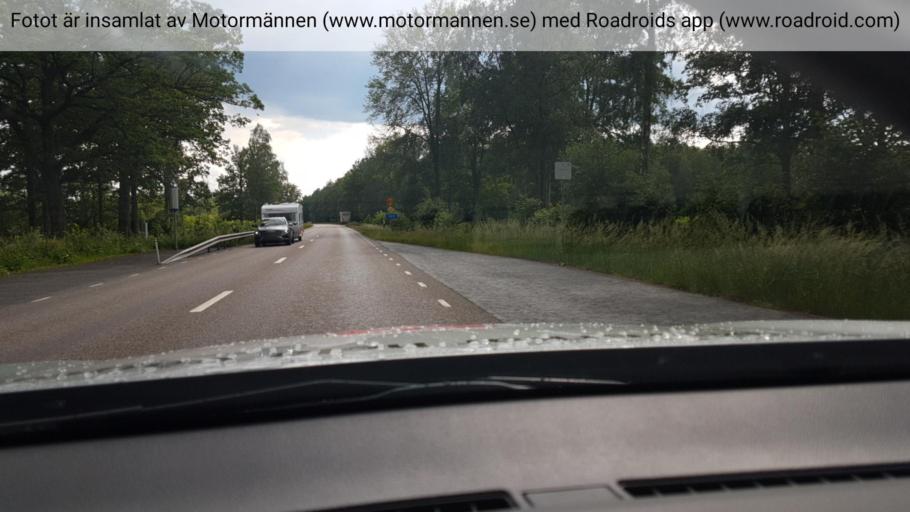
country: SE
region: Vaestra Goetaland
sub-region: Hjo Kommun
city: Hjo
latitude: 58.2254
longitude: 14.2103
